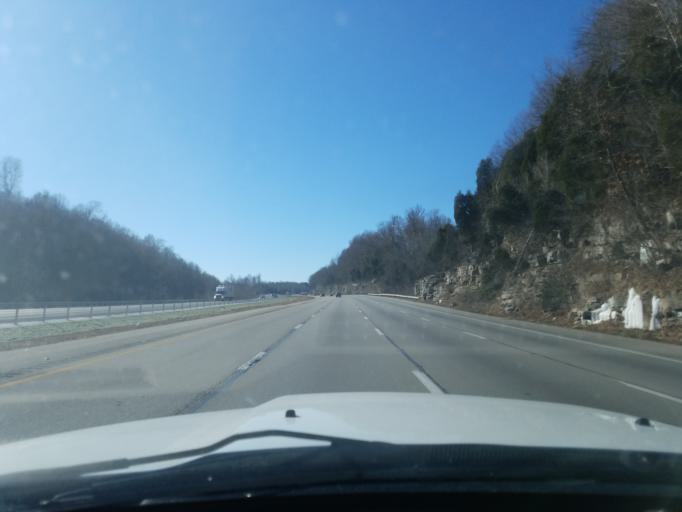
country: US
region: Kentucky
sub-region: Hardin County
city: Elizabethtown
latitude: 37.7409
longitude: -85.7989
